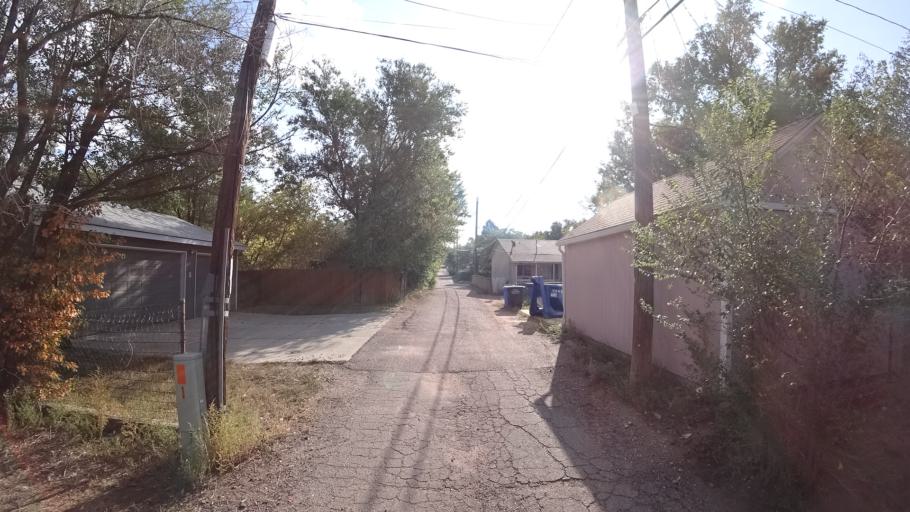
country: US
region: Colorado
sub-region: El Paso County
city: Colorado Springs
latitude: 38.8257
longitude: -104.8089
